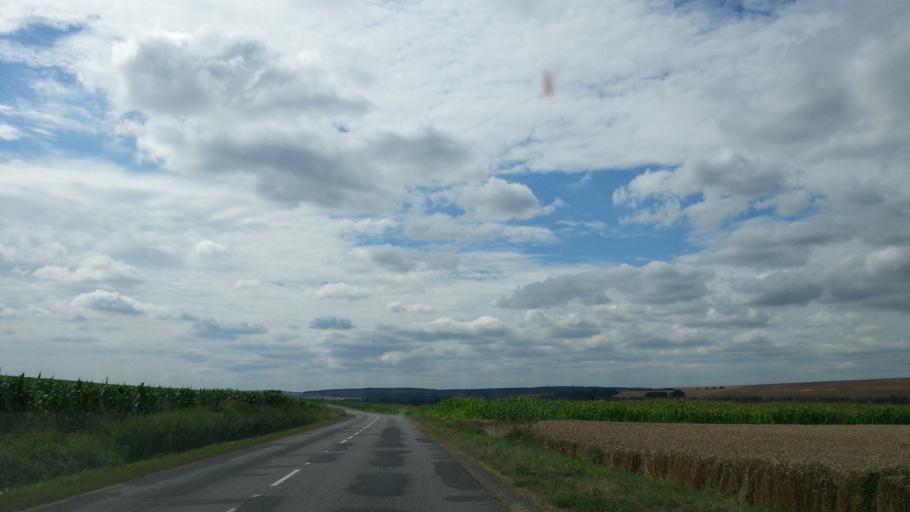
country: FR
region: Lorraine
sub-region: Departement de la Meuse
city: Thierville-sur-Meuse
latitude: 49.2107
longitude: 5.3469
